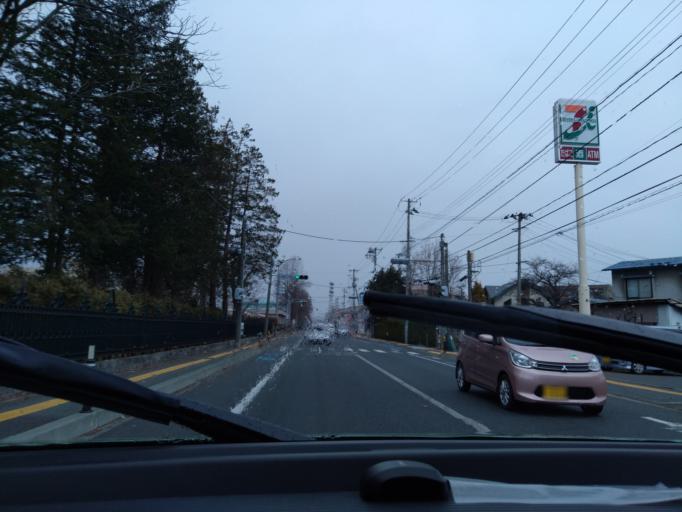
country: JP
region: Iwate
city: Morioka-shi
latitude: 39.7150
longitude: 141.1398
